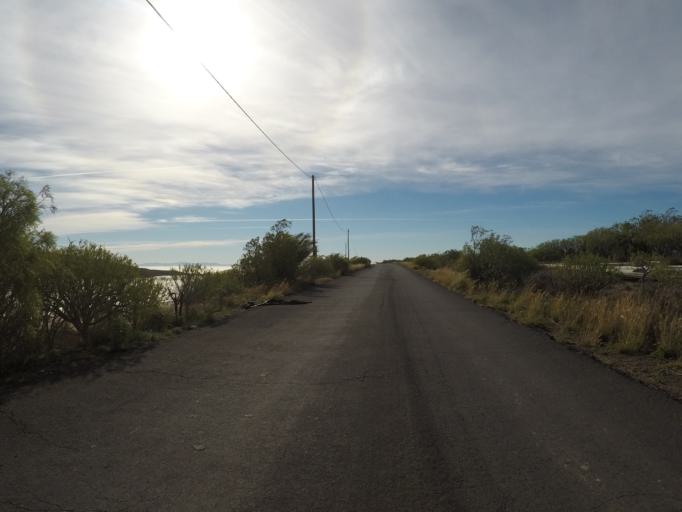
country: ES
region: Canary Islands
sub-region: Provincia de Santa Cruz de Tenerife
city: Lomo de Arico
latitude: 28.1522
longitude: -16.4912
